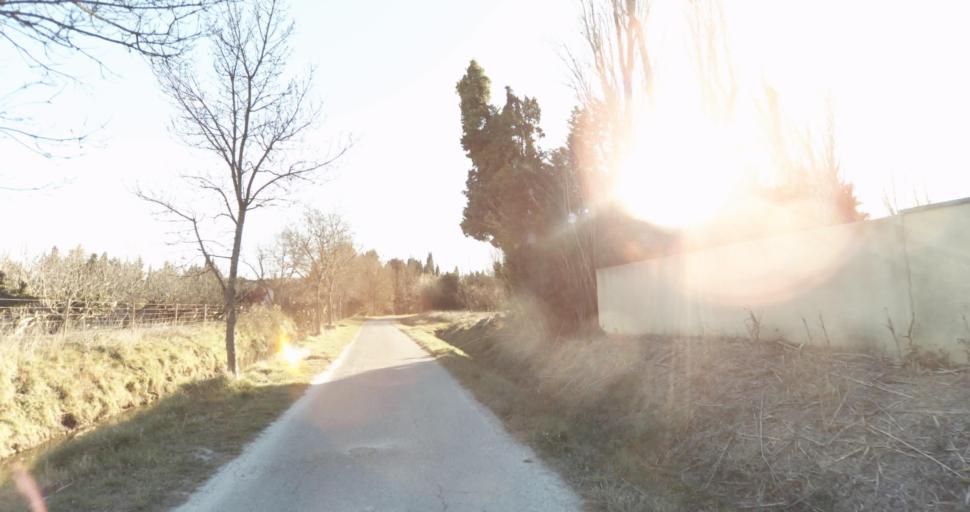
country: FR
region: Provence-Alpes-Cote d'Azur
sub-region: Departement des Bouches-du-Rhone
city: Barbentane
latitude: 43.9035
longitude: 4.7390
